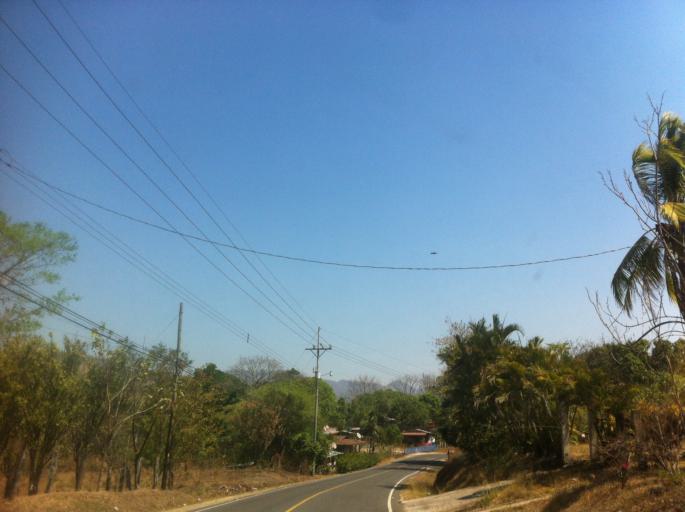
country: CR
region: Guanacaste
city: Hojancha
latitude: 10.0208
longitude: -85.5023
